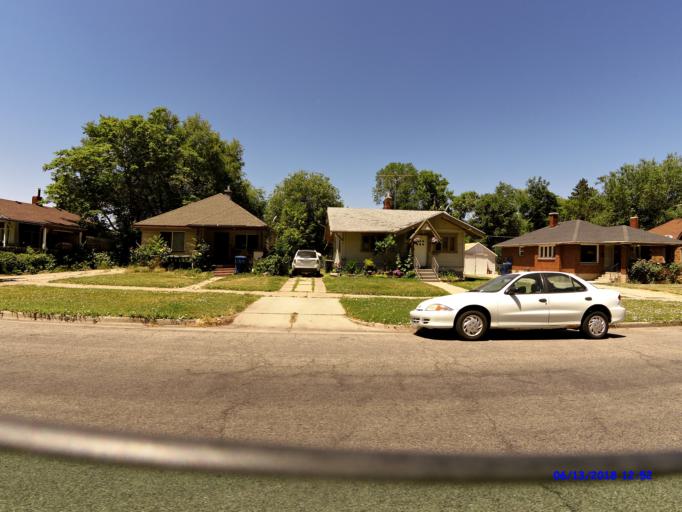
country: US
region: Utah
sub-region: Weber County
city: Ogden
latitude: 41.2114
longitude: -111.9595
